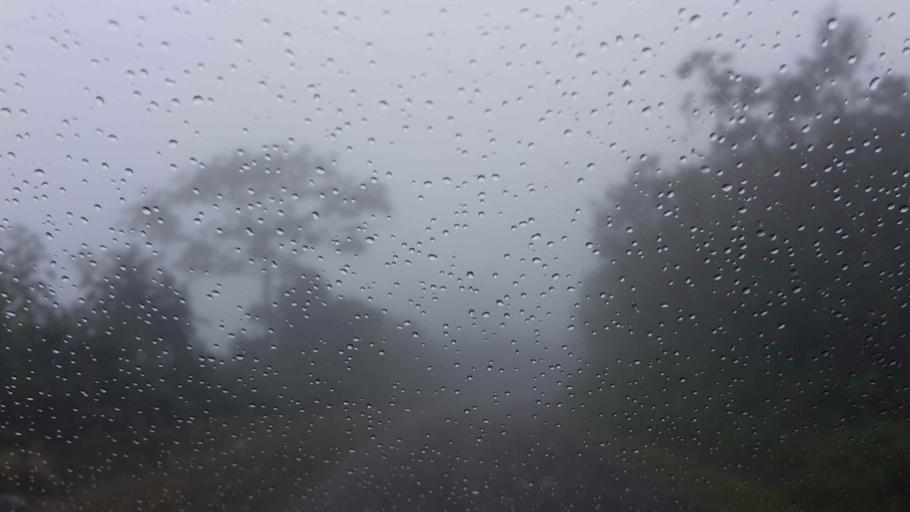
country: BO
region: Cochabamba
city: Colomi
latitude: -17.0923
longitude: -65.9907
